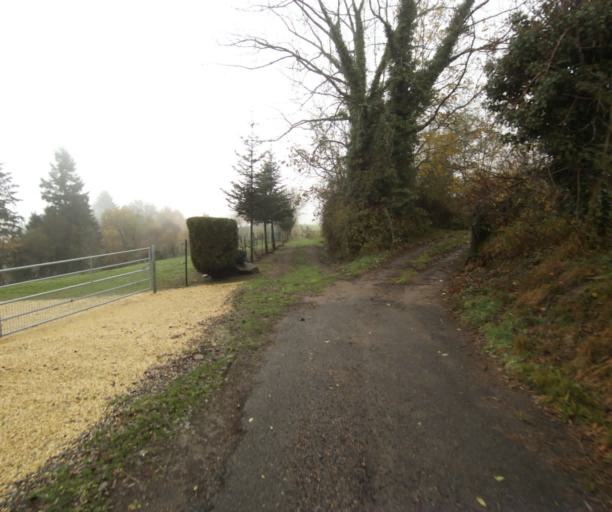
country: FR
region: Limousin
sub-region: Departement de la Correze
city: Cornil
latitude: 45.1851
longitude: 1.6336
